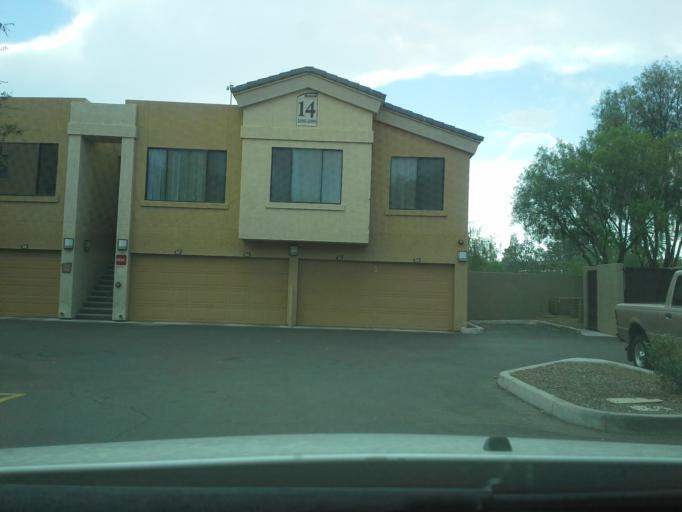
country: US
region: Arizona
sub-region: Maricopa County
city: Glendale
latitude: 33.6667
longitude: -112.1114
